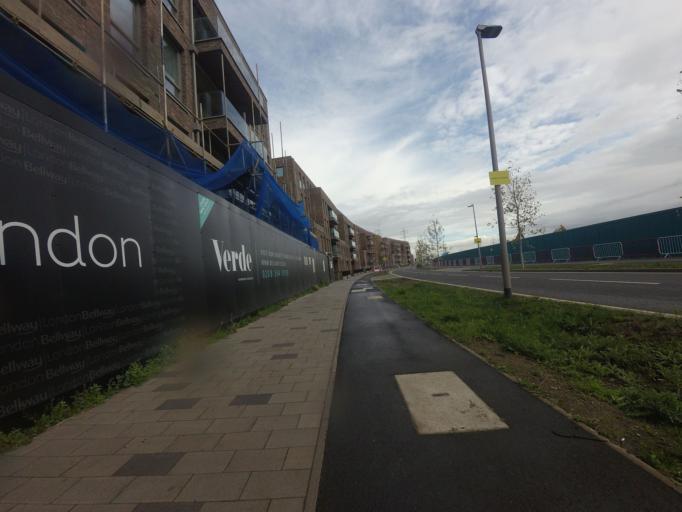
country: GB
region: England
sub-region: Greater London
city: Becontree
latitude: 51.5236
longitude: 0.1215
